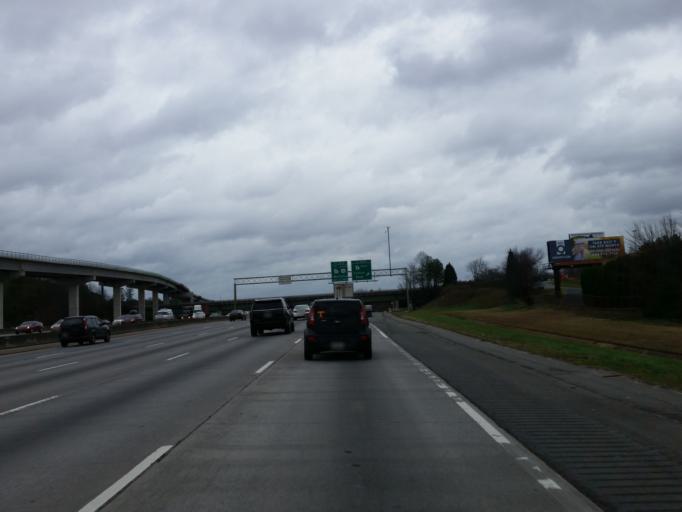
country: US
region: Georgia
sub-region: Cobb County
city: Marietta
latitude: 33.9793
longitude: -84.5367
